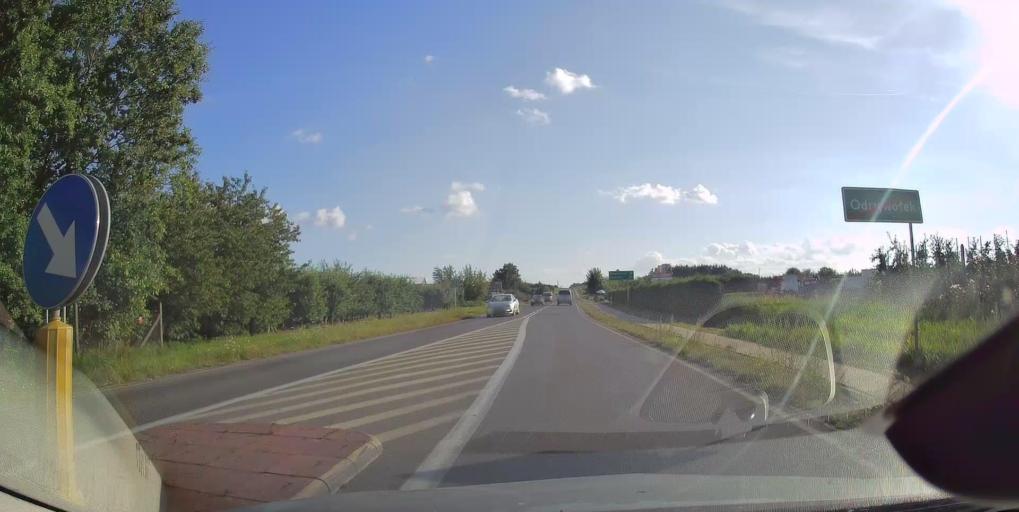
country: PL
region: Masovian Voivodeship
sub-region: Powiat grojecki
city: Belsk Duzy
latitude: 51.8444
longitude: 20.8332
